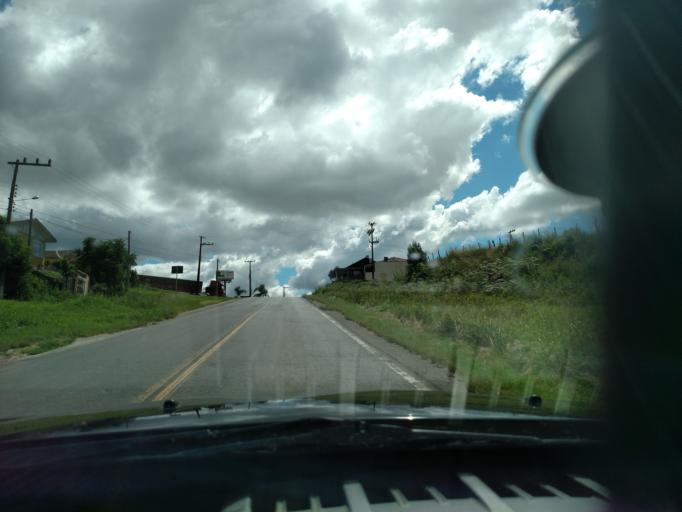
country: BR
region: Santa Catarina
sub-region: Lages
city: Lages
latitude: -27.8154
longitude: -50.2815
